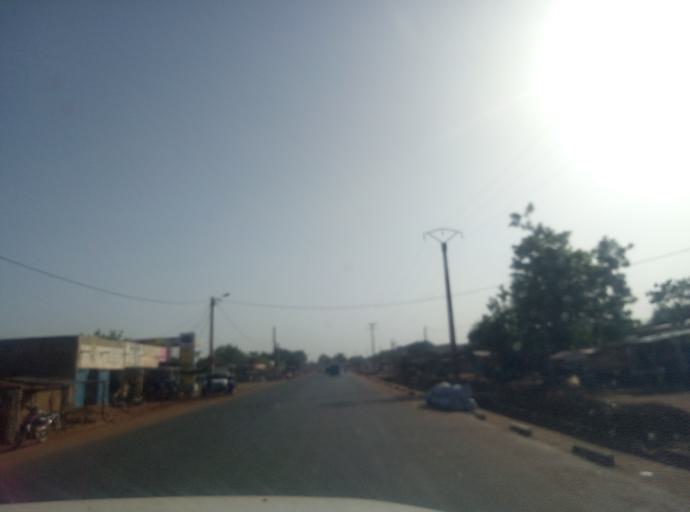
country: ML
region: Bamako
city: Bamako
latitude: 12.5868
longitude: -7.7672
